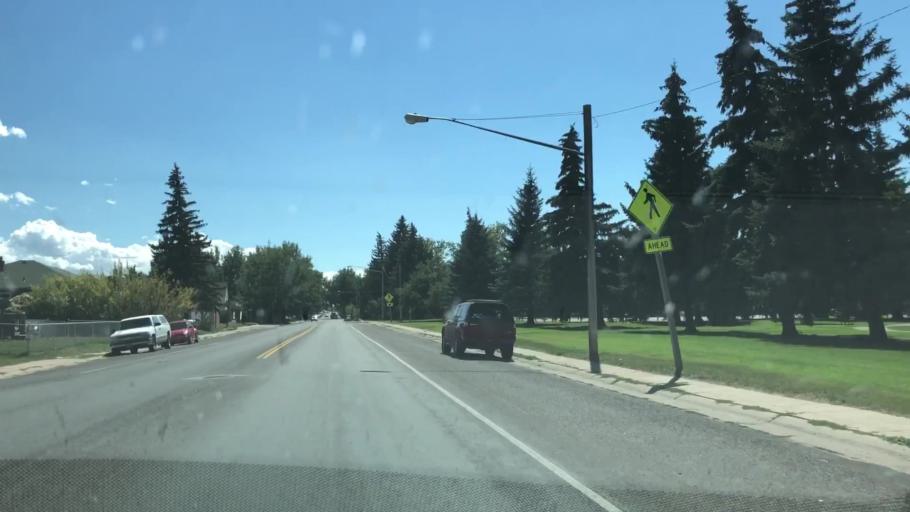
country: US
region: Wyoming
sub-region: Albany County
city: Laramie
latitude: 41.3220
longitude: -105.5845
